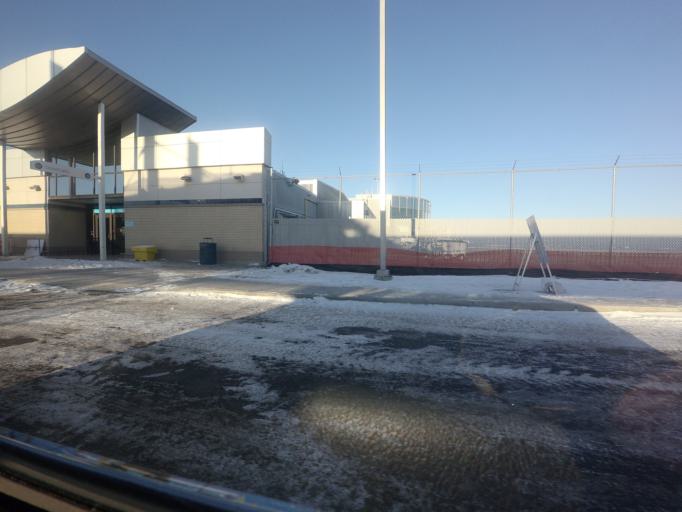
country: CA
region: Saskatchewan
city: Saskatoon
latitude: 52.1706
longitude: -106.6892
